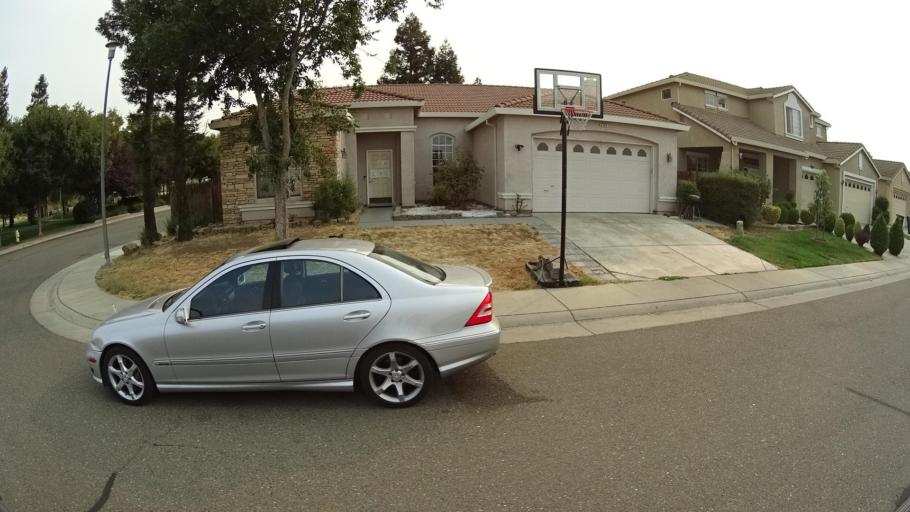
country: US
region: California
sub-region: Sacramento County
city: Laguna
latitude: 38.4291
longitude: -121.4080
